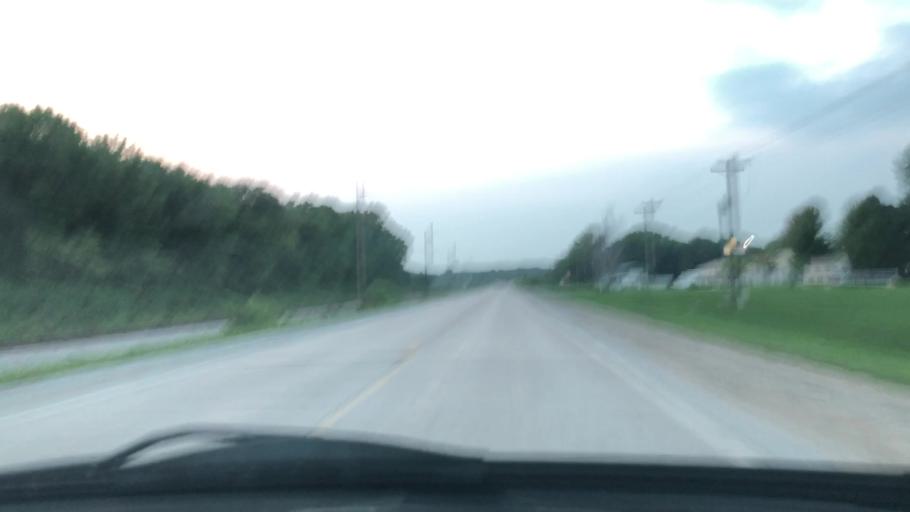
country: US
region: Iowa
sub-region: Johnson County
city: North Liberty
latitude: 41.8029
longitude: -91.6485
